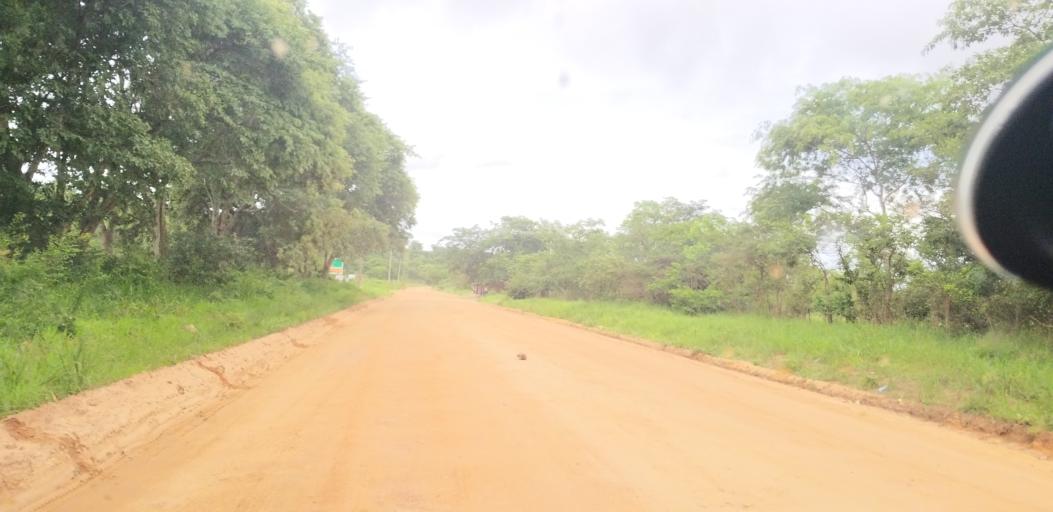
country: ZM
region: Lusaka
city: Lusaka
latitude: -15.1844
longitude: 28.4482
